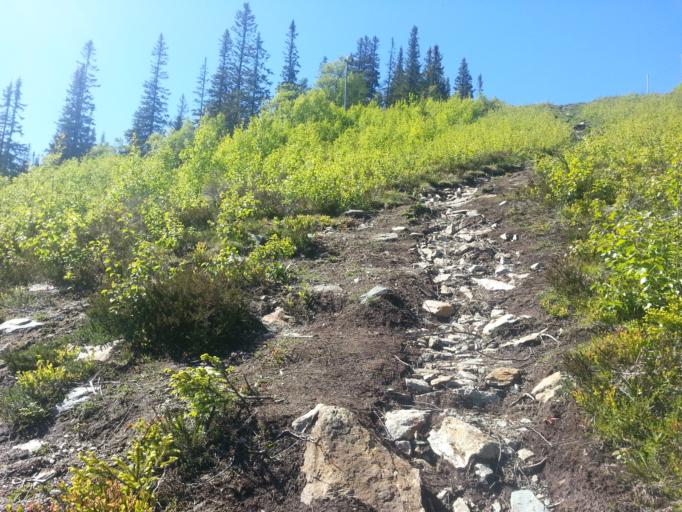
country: NO
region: Sor-Trondelag
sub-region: Melhus
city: Melhus
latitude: 63.4181
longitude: 10.2565
